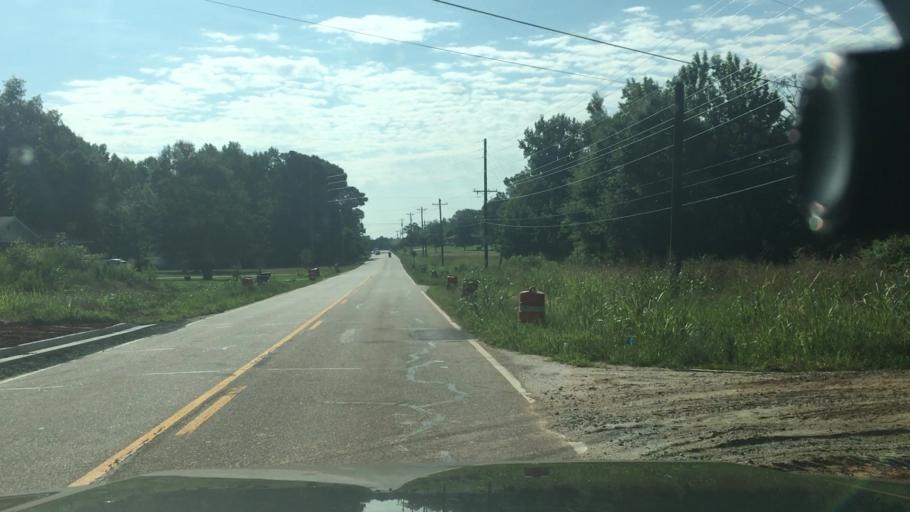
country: US
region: Georgia
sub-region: Coweta County
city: East Newnan
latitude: 33.3582
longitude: -84.7490
